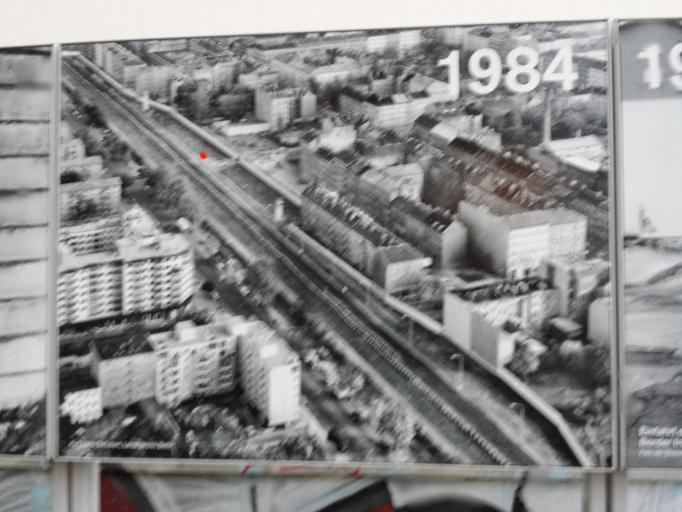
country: DE
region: Berlin
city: Gesundbrunnen
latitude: 52.5388
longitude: 13.3995
